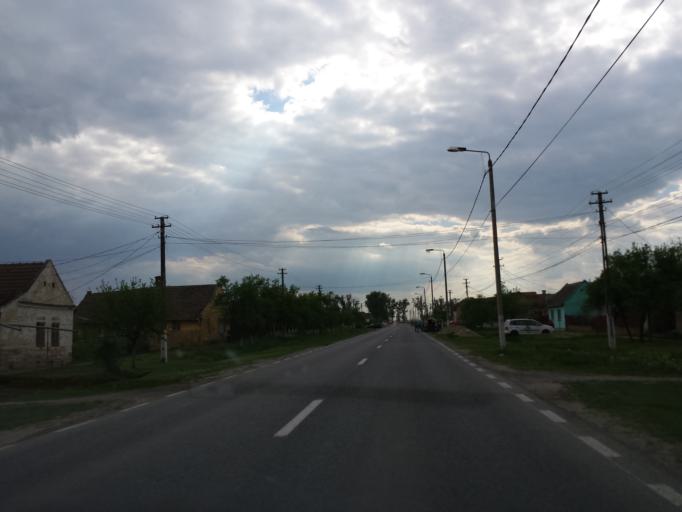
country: RO
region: Timis
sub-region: Comuna Cenad
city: Cenad
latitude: 46.1312
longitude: 20.5707
